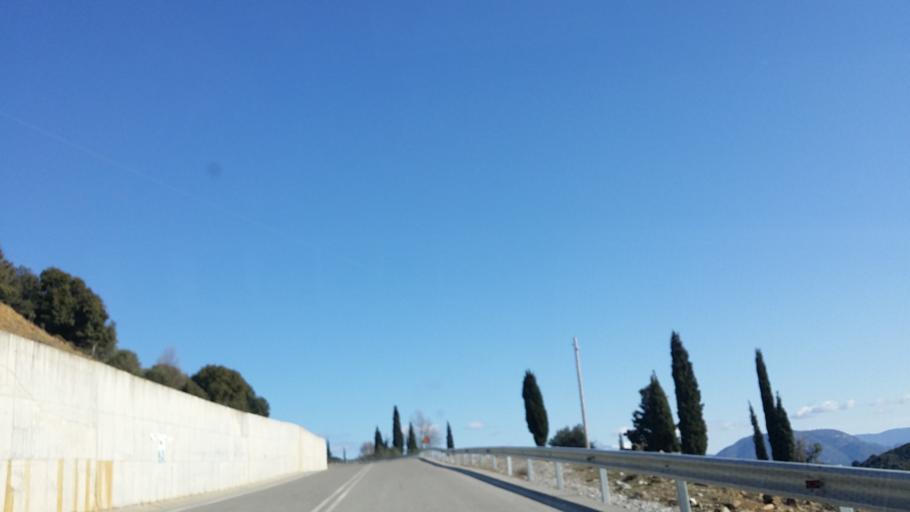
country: GR
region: Central Greece
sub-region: Nomos Evrytanias
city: Kerasochori
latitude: 38.9300
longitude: 21.4423
